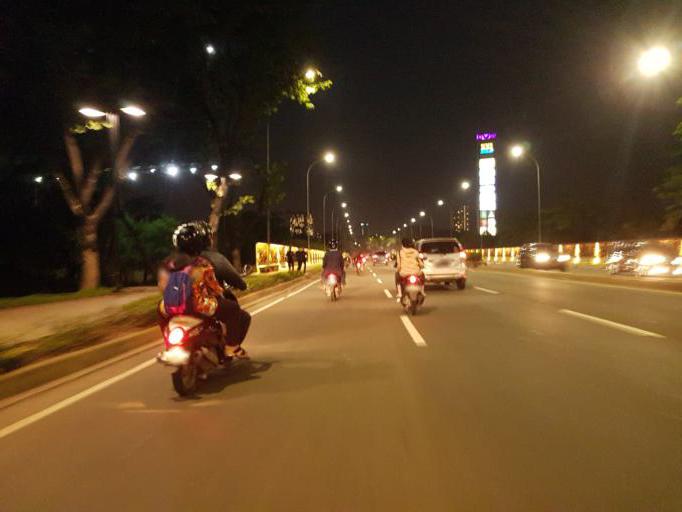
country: ID
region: West Java
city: Serpong
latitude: -6.2992
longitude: 106.6518
